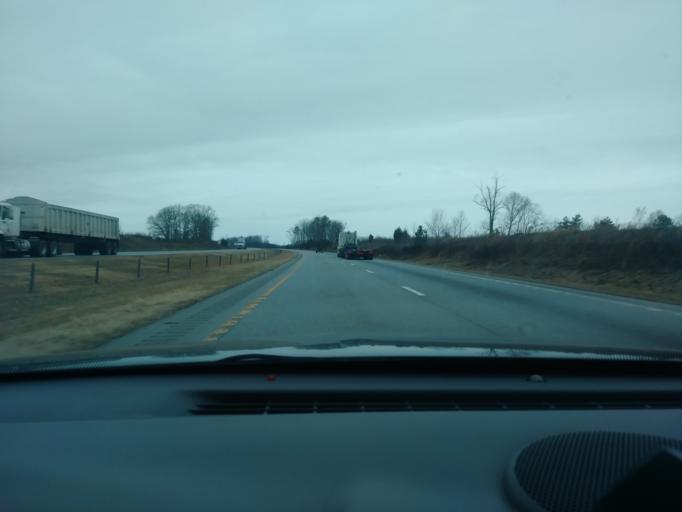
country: US
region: North Carolina
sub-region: Yadkin County
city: Jonesville
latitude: 36.1404
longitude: -80.8703
